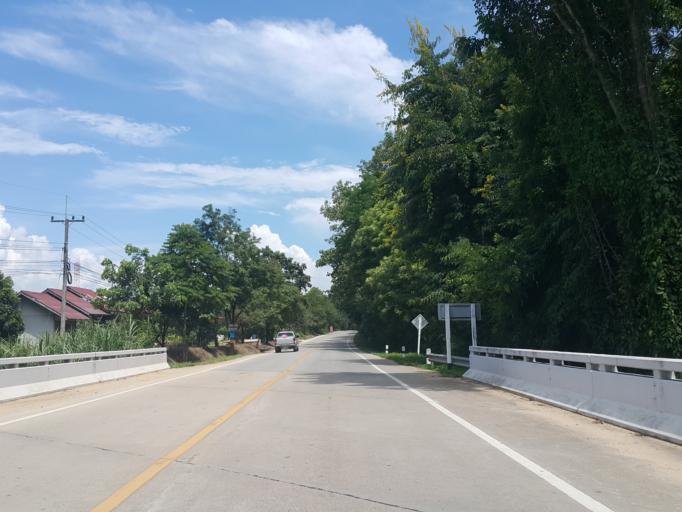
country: TH
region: Chiang Mai
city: Phrao
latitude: 19.2843
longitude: 99.1875
